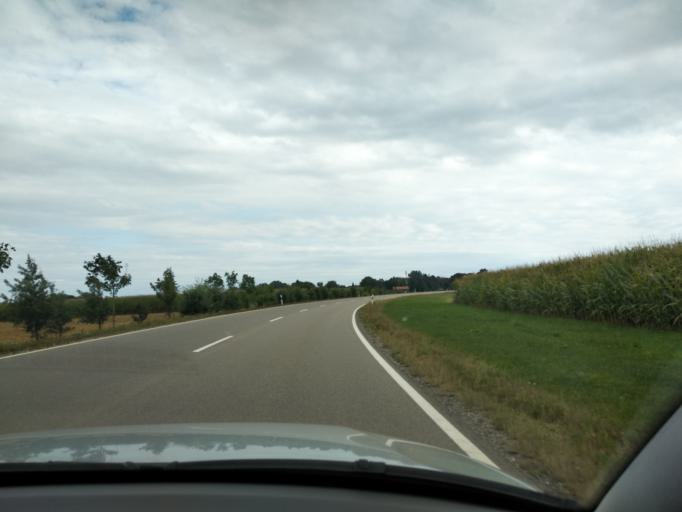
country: DE
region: Bavaria
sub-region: Swabia
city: Trunkelsberg
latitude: 47.9961
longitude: 10.2171
